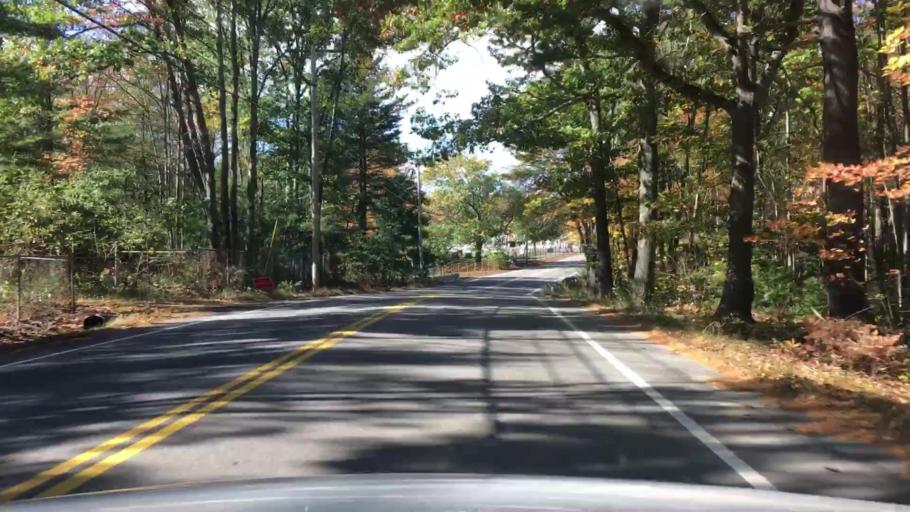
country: US
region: Maine
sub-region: York County
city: Biddeford
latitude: 43.4719
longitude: -70.4551
